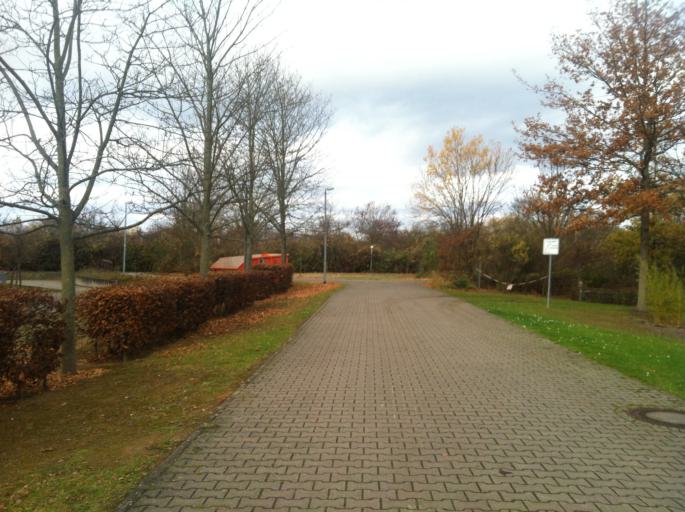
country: DE
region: Rheinland-Pfalz
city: Klein-Winternheim
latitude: 49.9945
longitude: 8.2225
